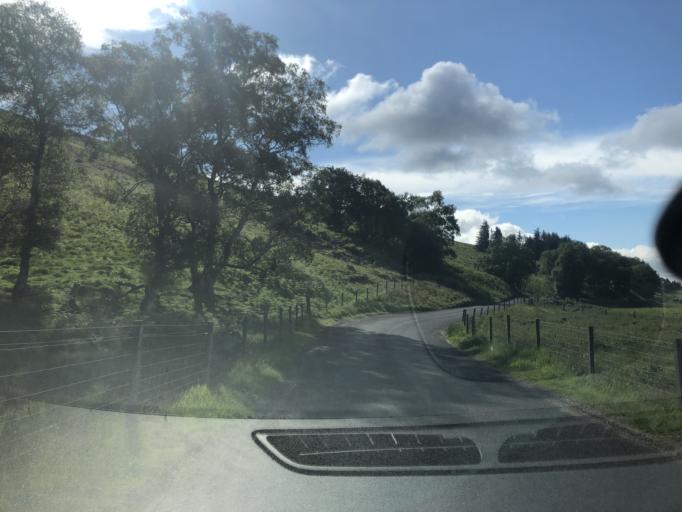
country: GB
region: Scotland
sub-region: Angus
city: Kirriemuir
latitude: 56.7887
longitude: -3.0307
